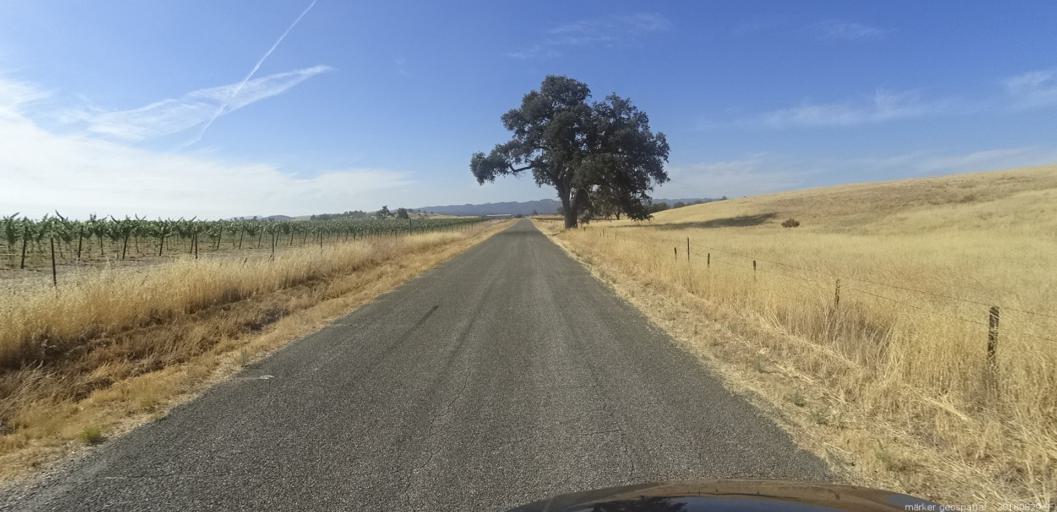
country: US
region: California
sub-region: Monterey County
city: King City
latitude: 35.9723
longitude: -121.1175
